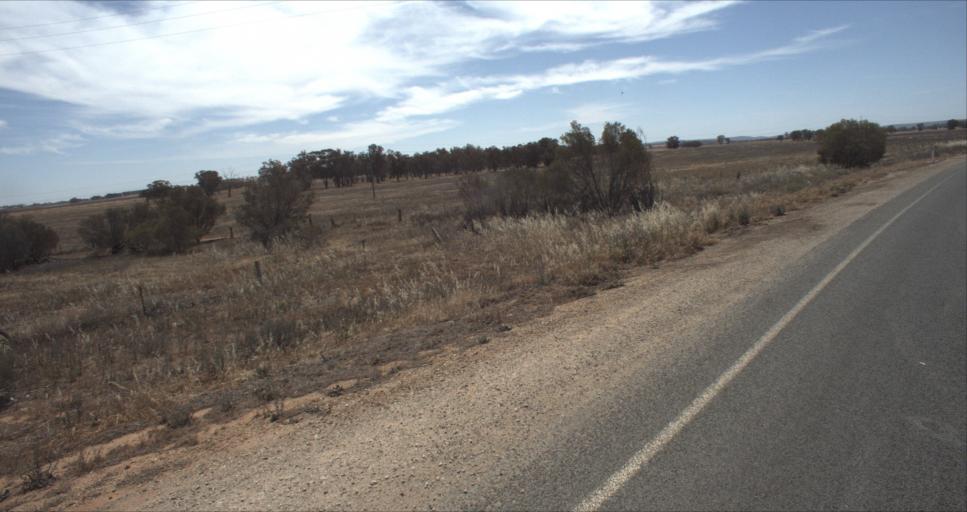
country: AU
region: New South Wales
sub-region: Leeton
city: Leeton
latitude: -34.6627
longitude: 146.4494
